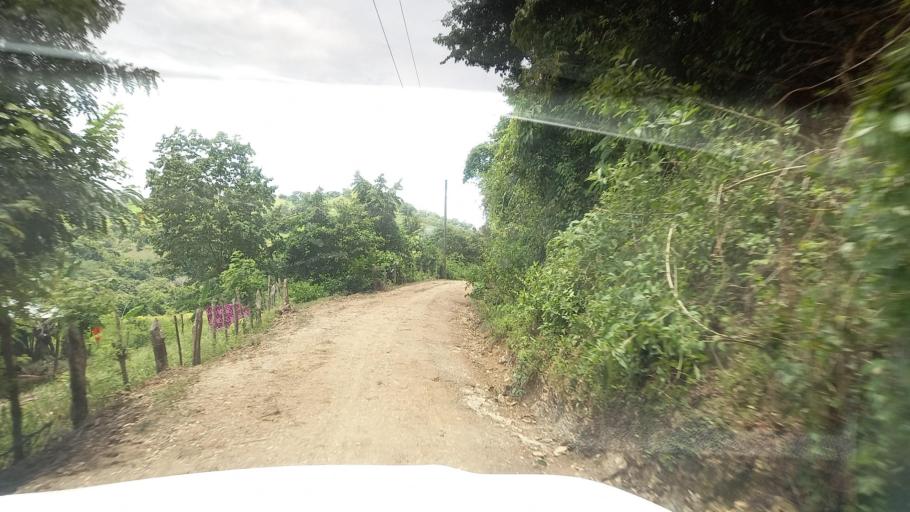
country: NI
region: Nueva Segovia
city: Wiwili
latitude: 13.7319
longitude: -85.7877
